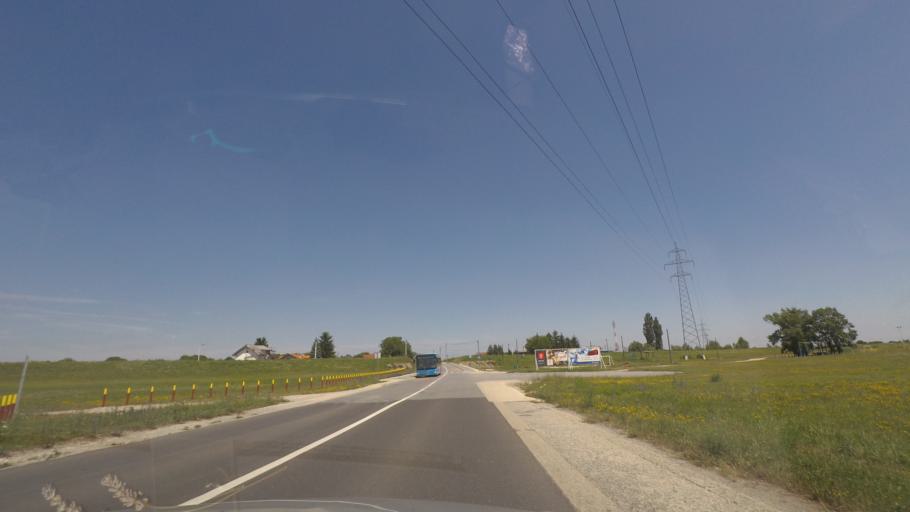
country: HR
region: Grad Zagreb
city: Zadvorsko
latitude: 45.7596
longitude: 15.9095
